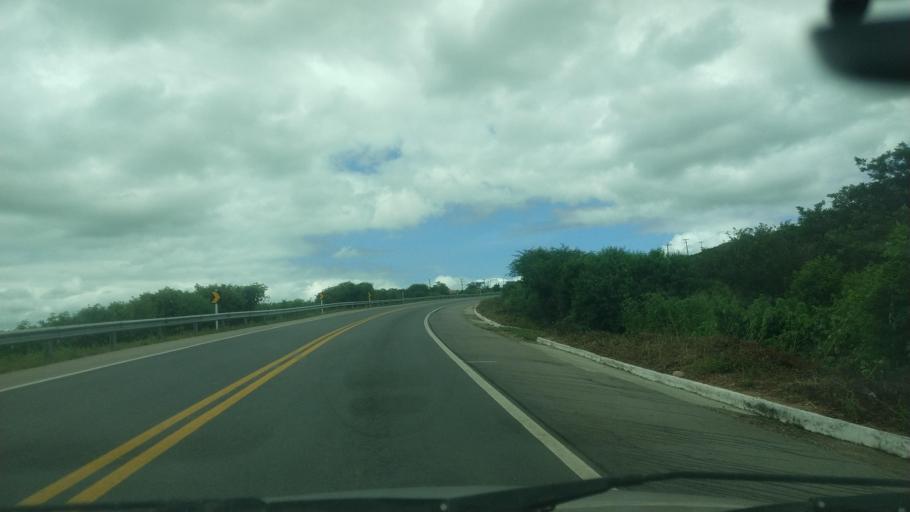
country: BR
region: Rio Grande do Norte
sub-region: Santa Cruz
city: Santa Cruz
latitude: -6.2182
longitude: -36.1617
